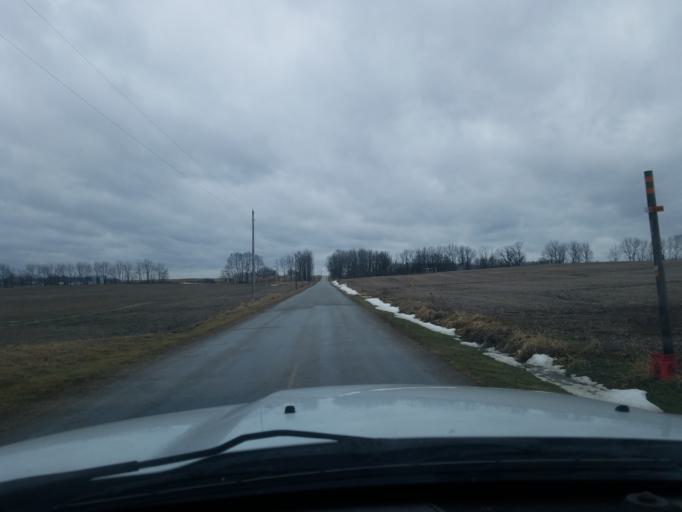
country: US
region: Indiana
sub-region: Noble County
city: Rome City
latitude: 41.4489
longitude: -85.3948
